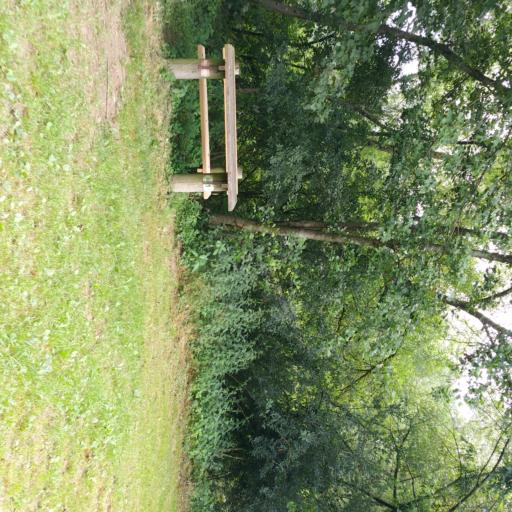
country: AT
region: Styria
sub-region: Politischer Bezirk Leibnitz
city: Gleinstatten
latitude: 46.7524
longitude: 15.3900
